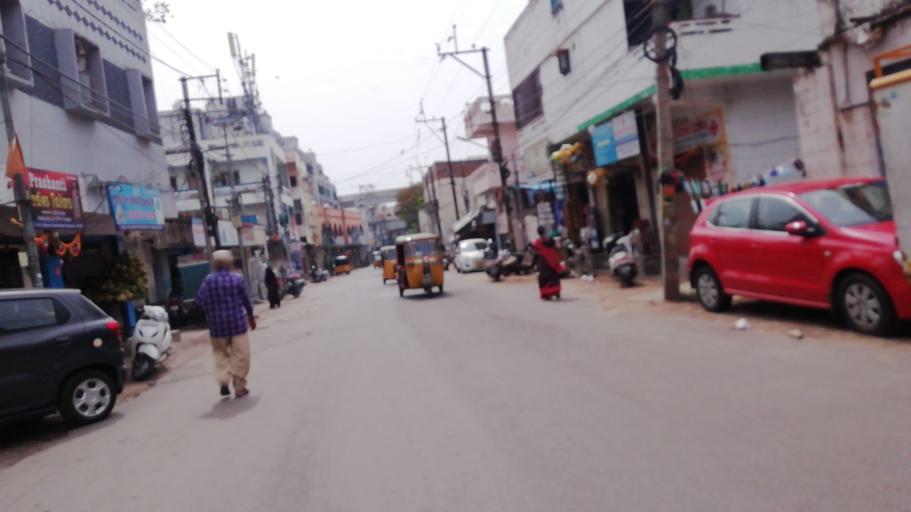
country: IN
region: Telangana
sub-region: Hyderabad
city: Malkajgiri
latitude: 17.4150
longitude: 78.5001
